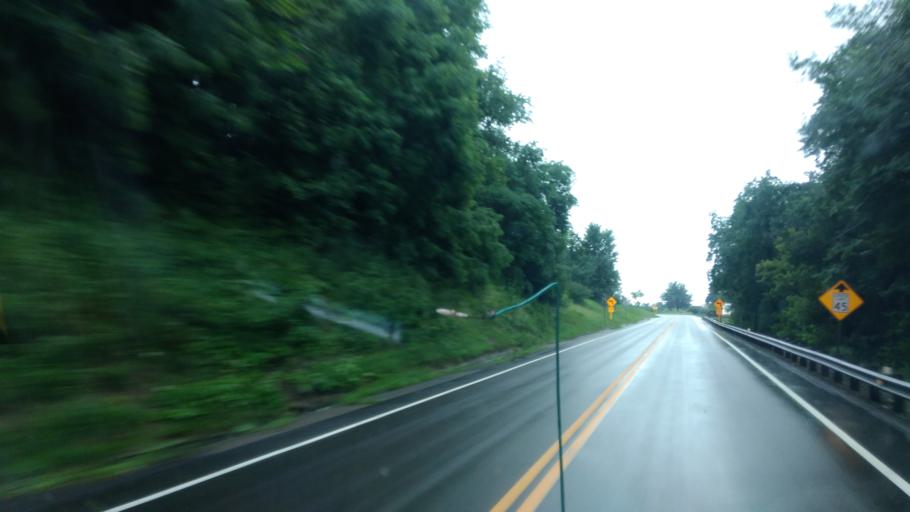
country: US
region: Ohio
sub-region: Carroll County
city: Carrollton
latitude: 40.5712
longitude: -81.0768
